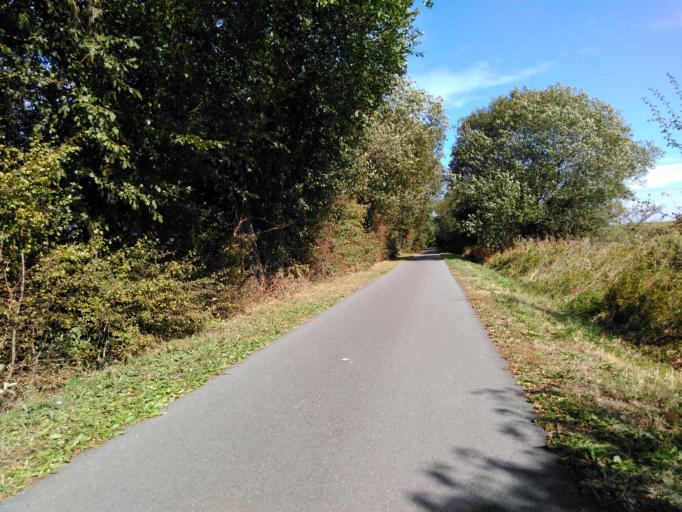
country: BE
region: Wallonia
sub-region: Province du Luxembourg
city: Bastogne
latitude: 50.0184
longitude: 5.7412
